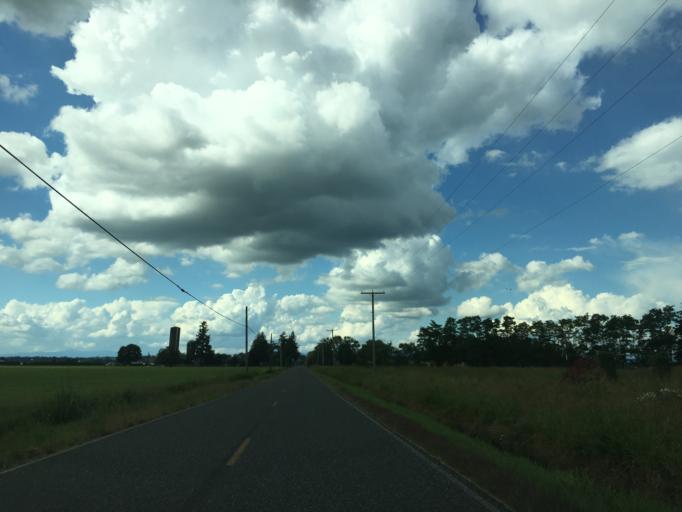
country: US
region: Washington
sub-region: Whatcom County
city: Lynden
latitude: 48.9740
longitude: -122.4738
